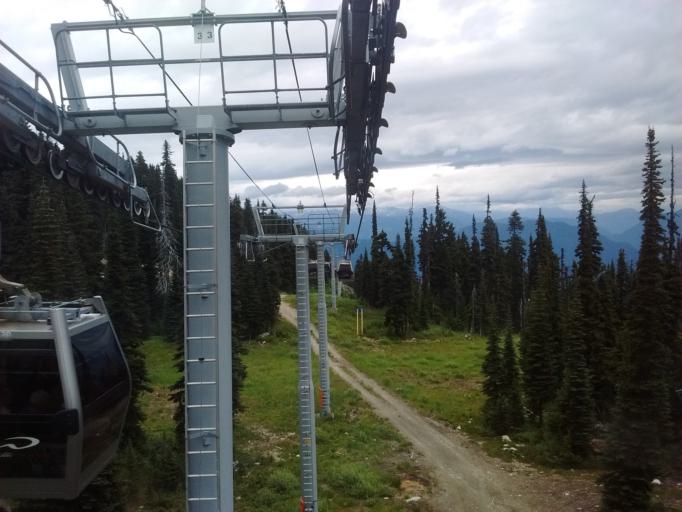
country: CA
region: British Columbia
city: Whistler
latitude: 50.0767
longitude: -122.9481
